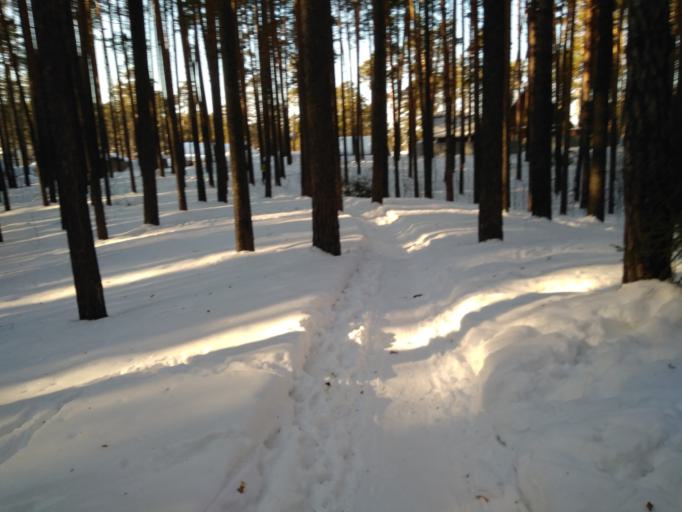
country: RU
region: Tomsk
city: Timiryazevskoye
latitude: 56.4867
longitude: 84.8795
